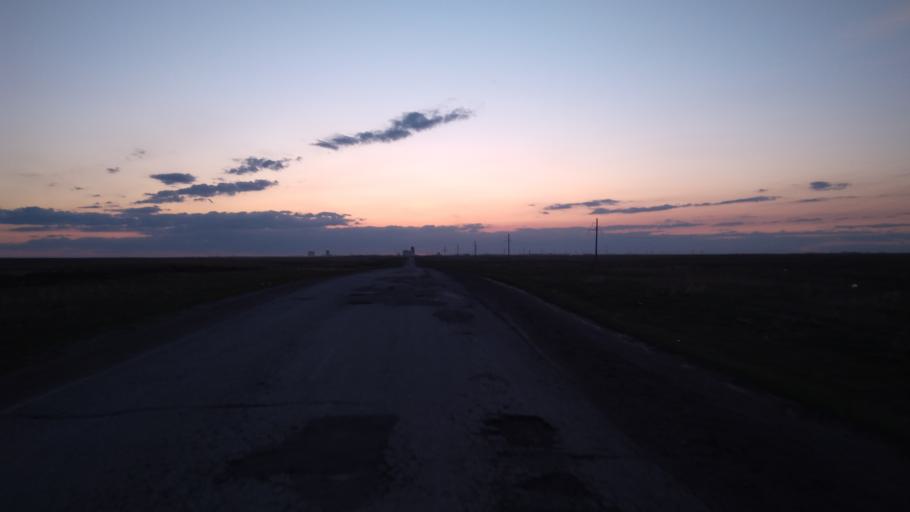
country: RU
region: Chelyabinsk
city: Troitsk
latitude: 54.0887
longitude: 61.6522
